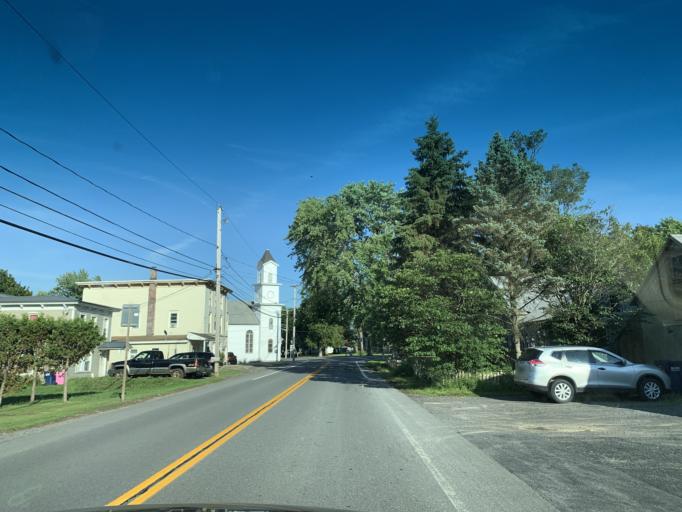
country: US
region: New York
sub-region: Oneida County
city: Vernon
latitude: 43.0535
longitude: -75.5033
